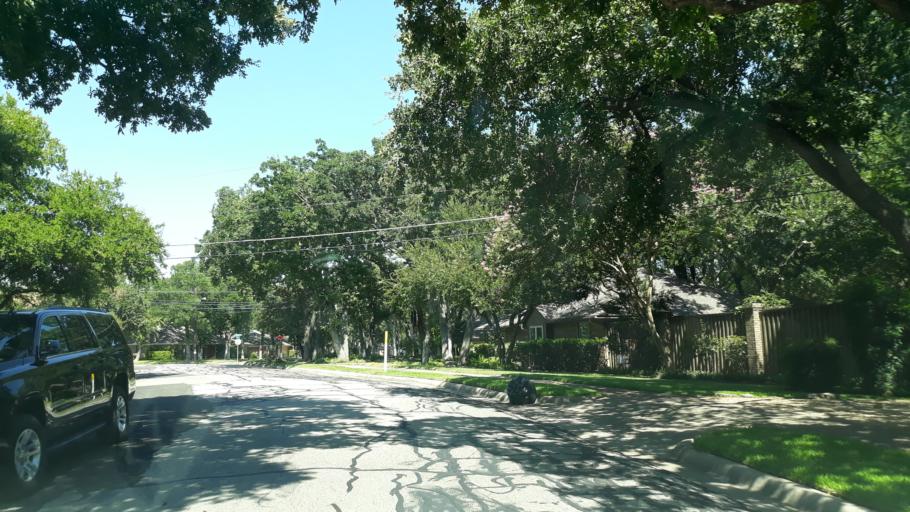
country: US
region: Texas
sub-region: Dallas County
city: Irving
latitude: 32.8272
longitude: -97.0052
